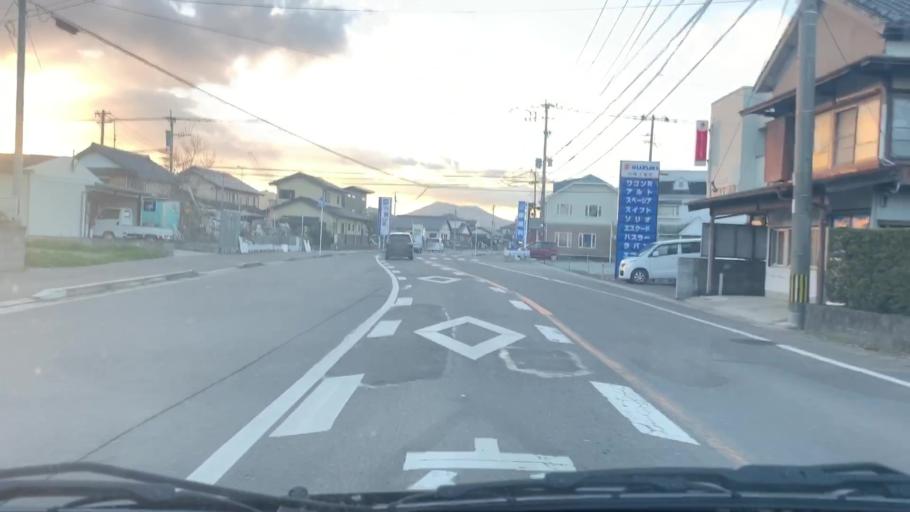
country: JP
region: Saga Prefecture
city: Kashima
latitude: 33.1867
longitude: 130.1400
